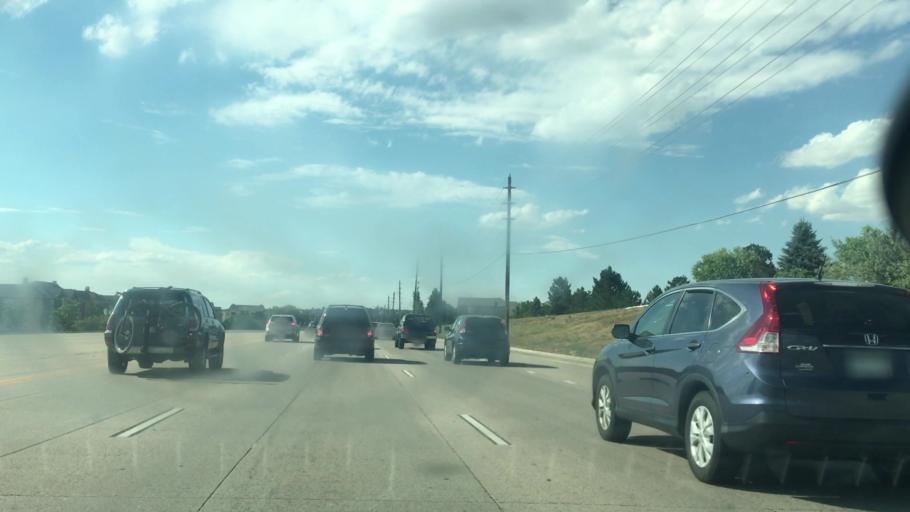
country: US
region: Colorado
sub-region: Arapahoe County
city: Dove Valley
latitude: 39.6046
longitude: -104.8074
